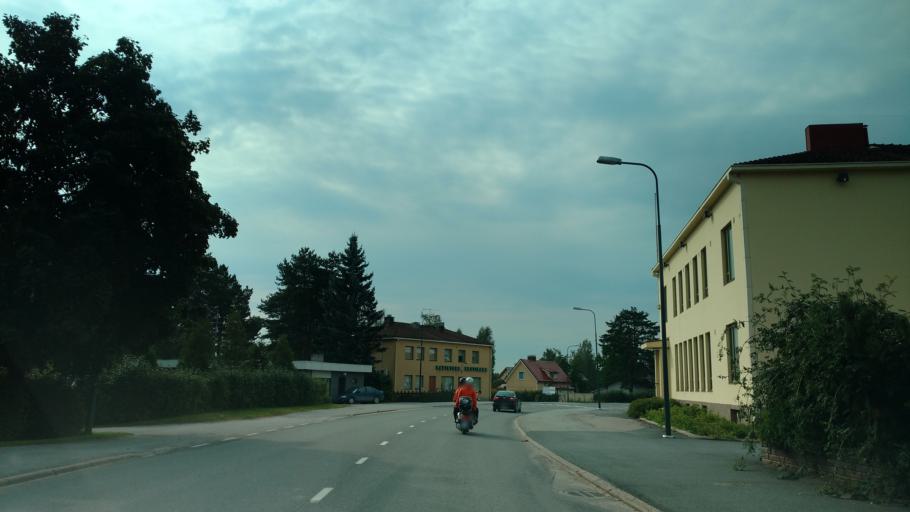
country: FI
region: Varsinais-Suomi
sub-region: Loimaa
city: Koski Tl
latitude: 60.6540
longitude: 23.1407
